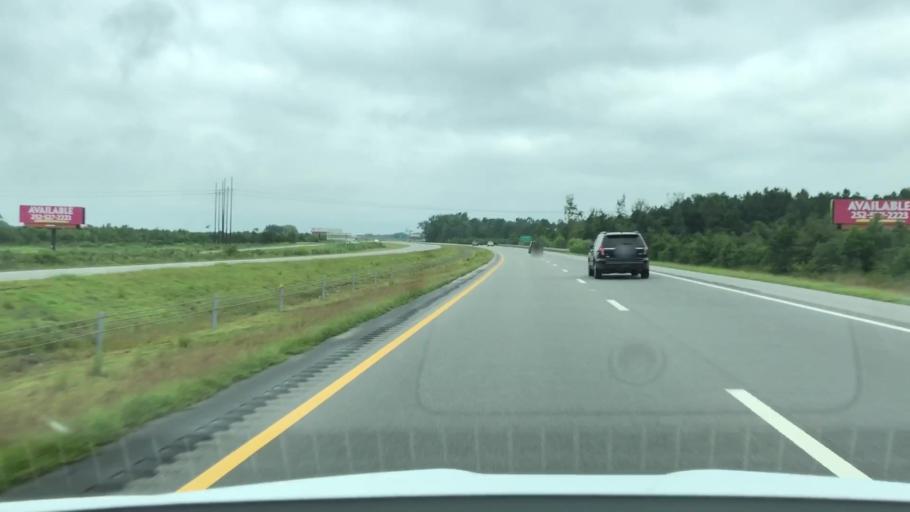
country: US
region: North Carolina
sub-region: Wayne County
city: Elroy
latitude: 35.3972
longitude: -77.8701
